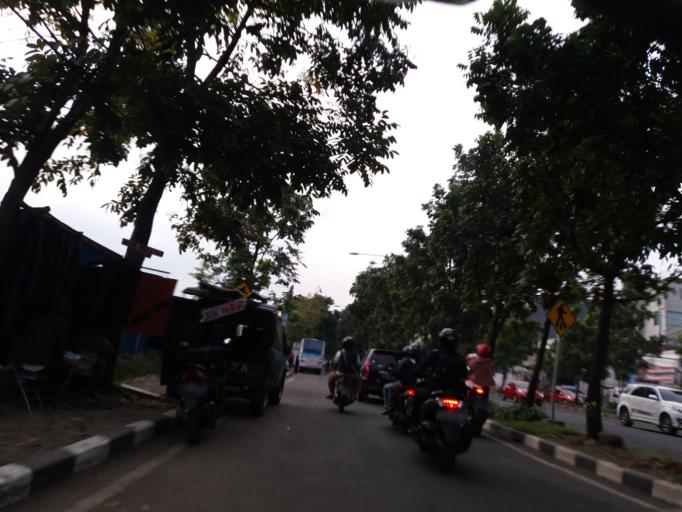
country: ID
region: West Java
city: Bandung
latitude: -6.9171
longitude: 107.6439
